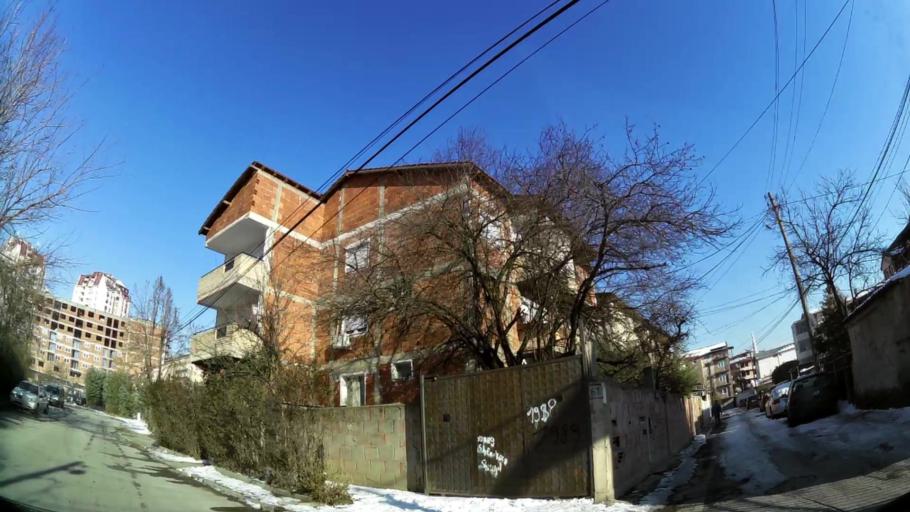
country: MK
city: Krushopek
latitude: 42.0036
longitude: 21.3809
